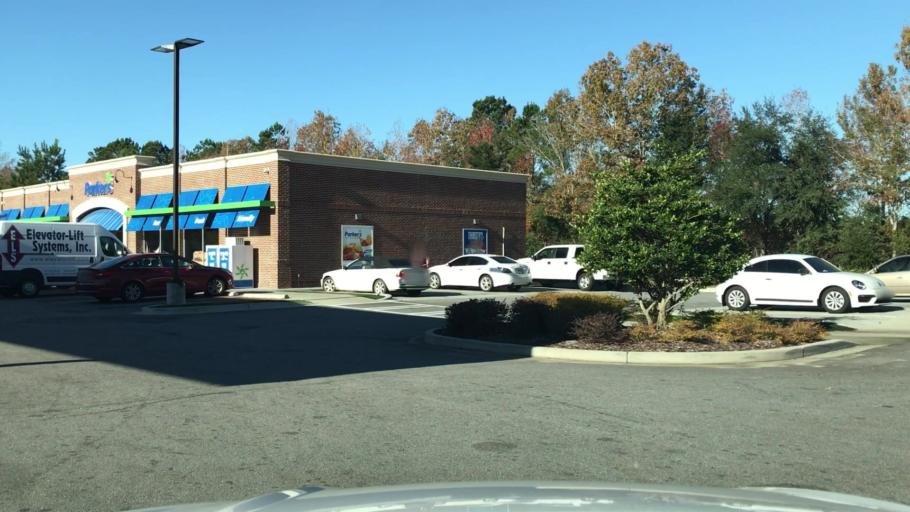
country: US
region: South Carolina
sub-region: Beaufort County
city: Laurel Bay
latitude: 32.3633
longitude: -80.8699
